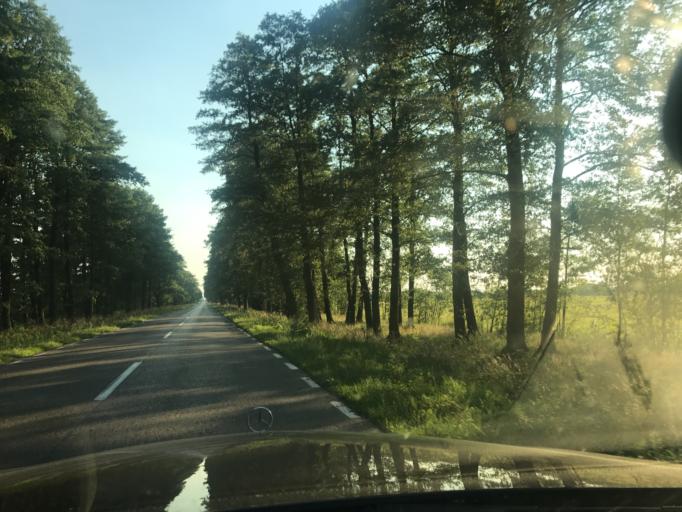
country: PL
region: Lublin Voivodeship
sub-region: Powiat parczewski
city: Jablon
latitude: 51.7432
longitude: 23.1480
